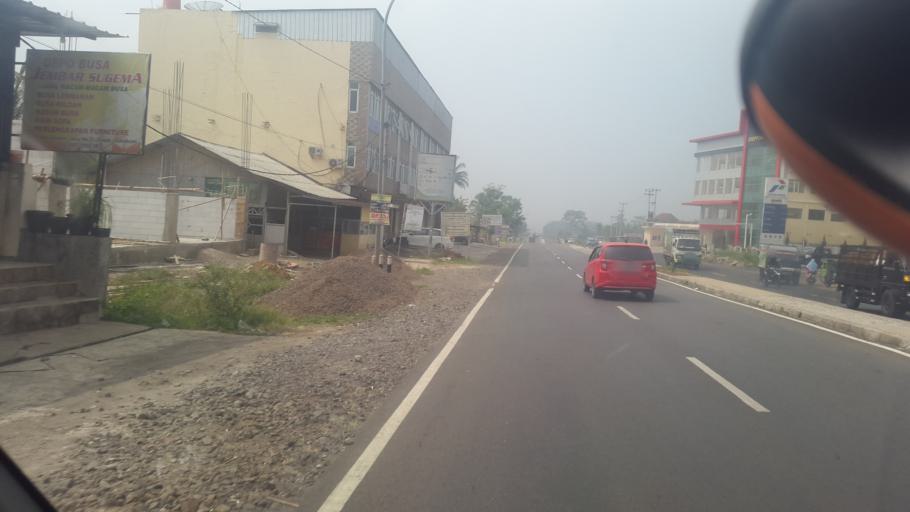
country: ID
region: West Java
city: Sukabumi
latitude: -6.9254
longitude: 106.8950
